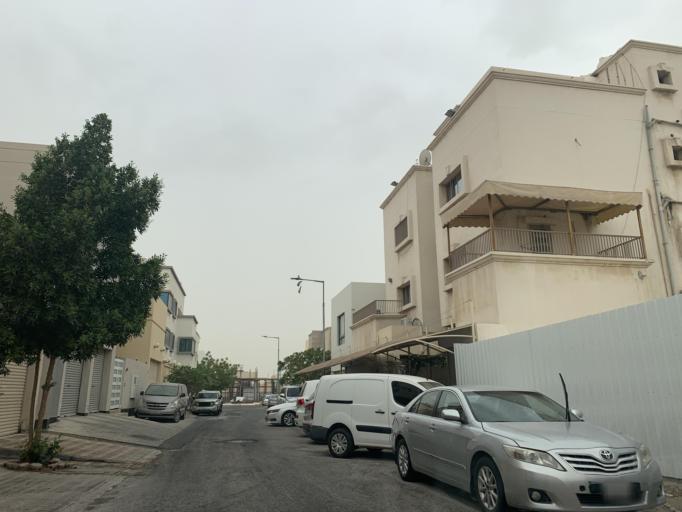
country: BH
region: Northern
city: Ar Rifa'
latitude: 26.1454
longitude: 50.5312
